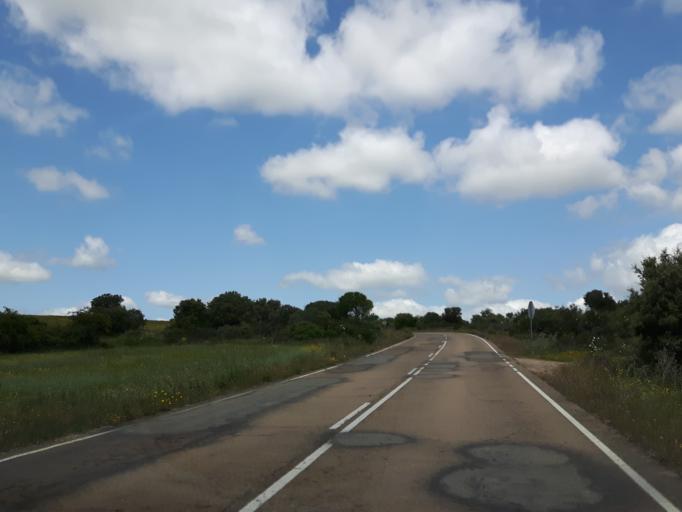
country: ES
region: Castille and Leon
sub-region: Provincia de Salamanca
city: Villar de la Yegua
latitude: 40.7148
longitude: -6.6872
